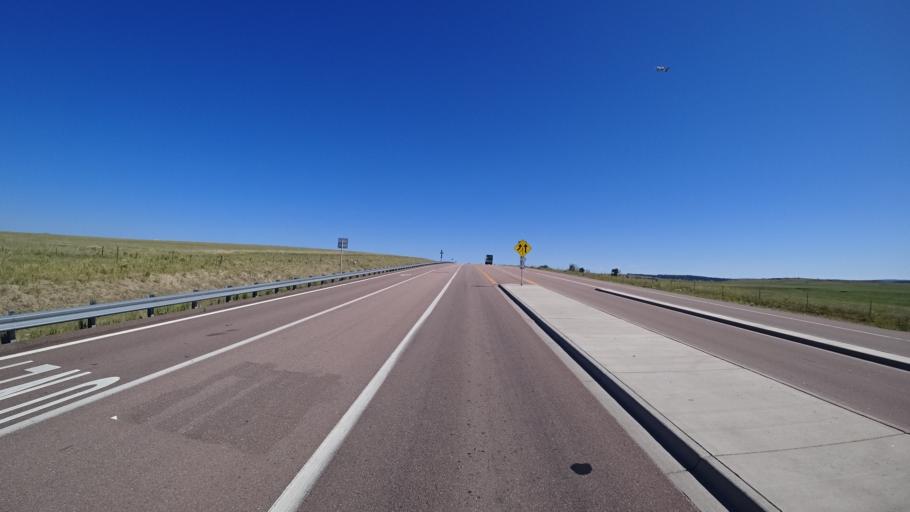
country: US
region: Colorado
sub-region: El Paso County
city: Cimarron Hills
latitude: 38.8269
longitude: -104.6827
